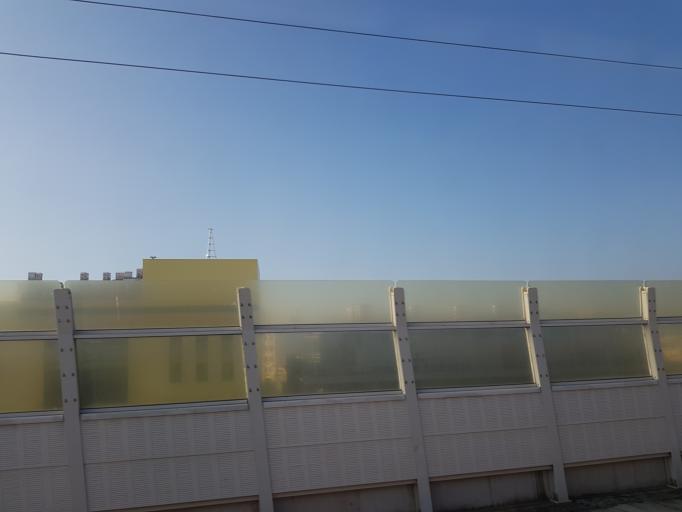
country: TW
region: Taiwan
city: Fengyuan
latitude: 24.2587
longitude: 120.7267
